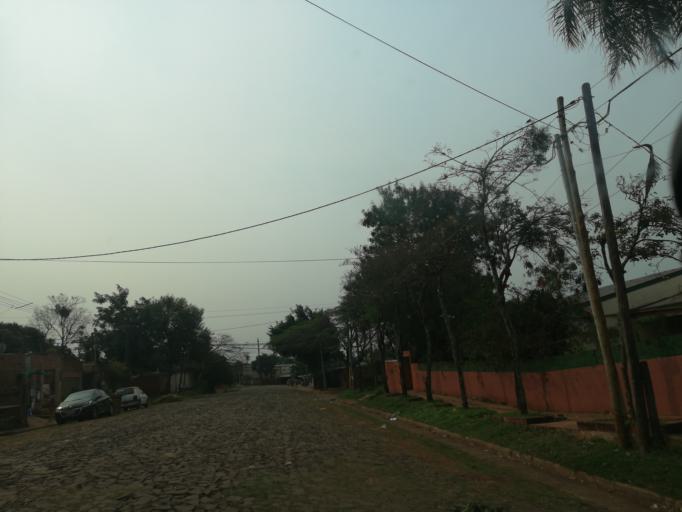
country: AR
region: Misiones
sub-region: Departamento de Capital
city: Posadas
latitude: -27.3749
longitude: -55.9383
